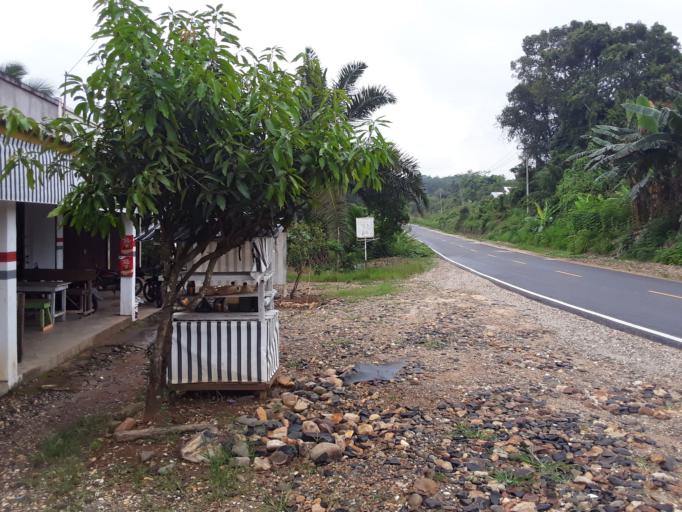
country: ID
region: Jambi
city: Bangko
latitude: -2.1344
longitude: 102.1820
